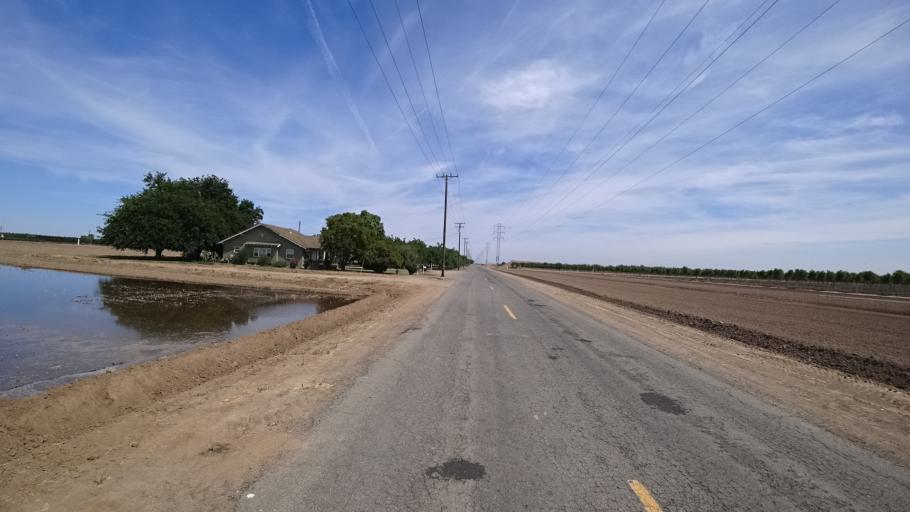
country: US
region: California
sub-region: Kings County
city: Hanford
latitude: 36.3517
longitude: -119.5921
